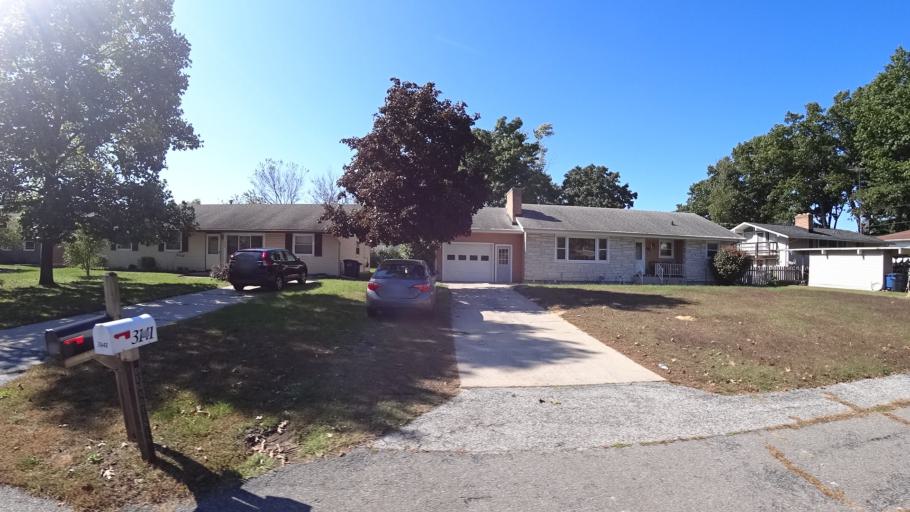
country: US
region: Indiana
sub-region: LaPorte County
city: Michigan City
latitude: 41.6924
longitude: -86.8843
